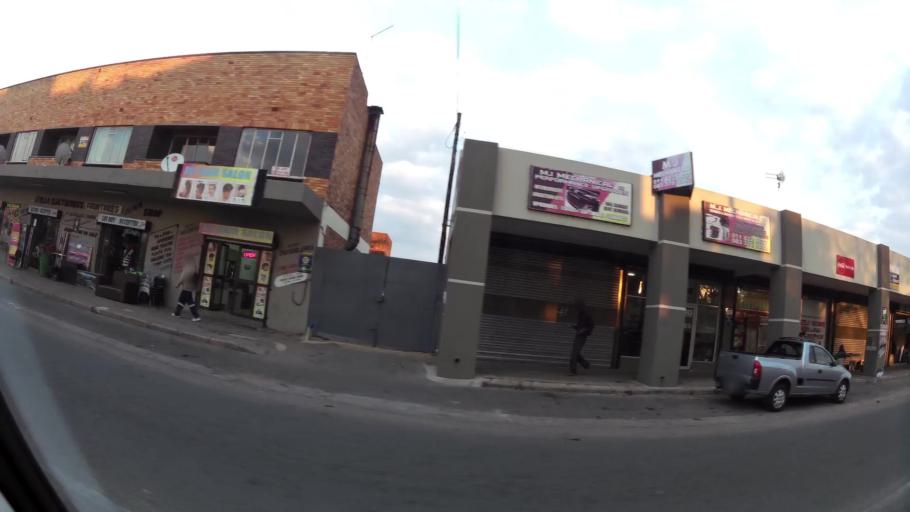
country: ZA
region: Gauteng
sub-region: Ekurhuleni Metropolitan Municipality
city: Germiston
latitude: -26.1854
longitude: 28.1701
